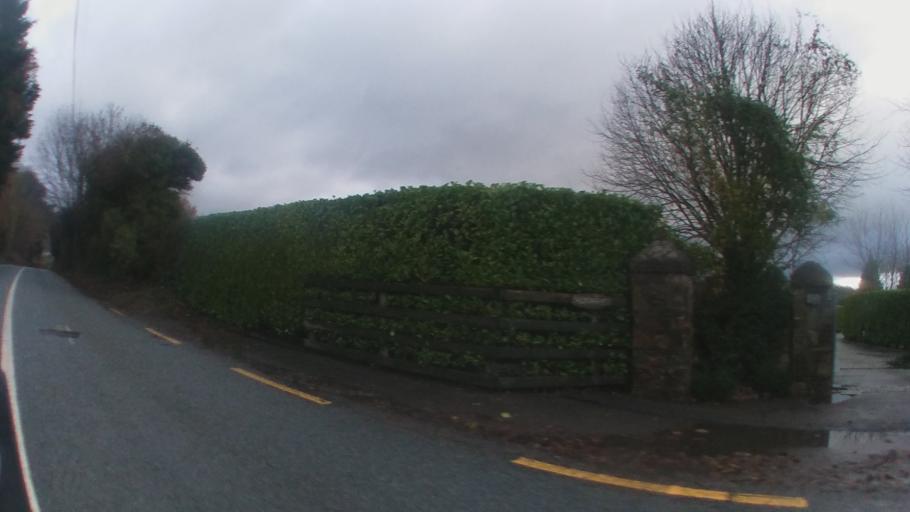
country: IE
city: Kilquade
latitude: 53.0951
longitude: -6.0964
